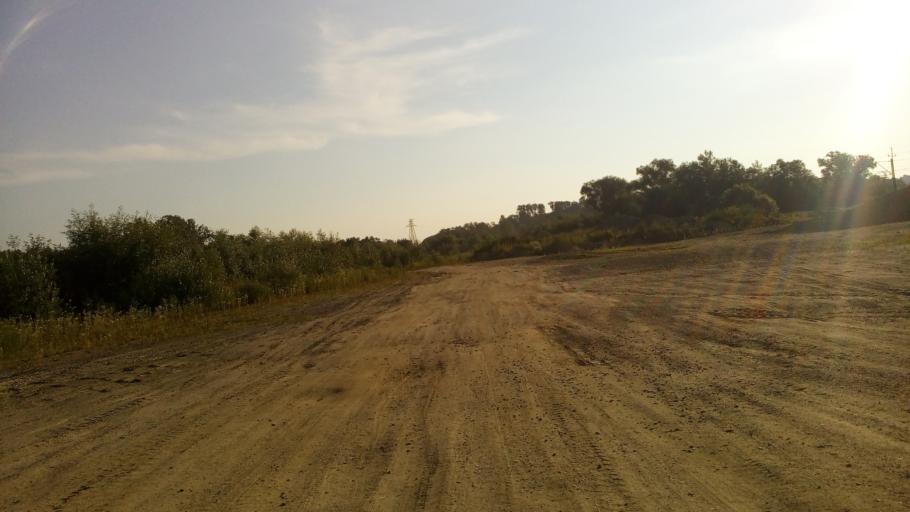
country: PL
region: Lesser Poland Voivodeship
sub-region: Powiat nowosadecki
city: Stary Sacz
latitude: 49.5739
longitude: 20.6472
